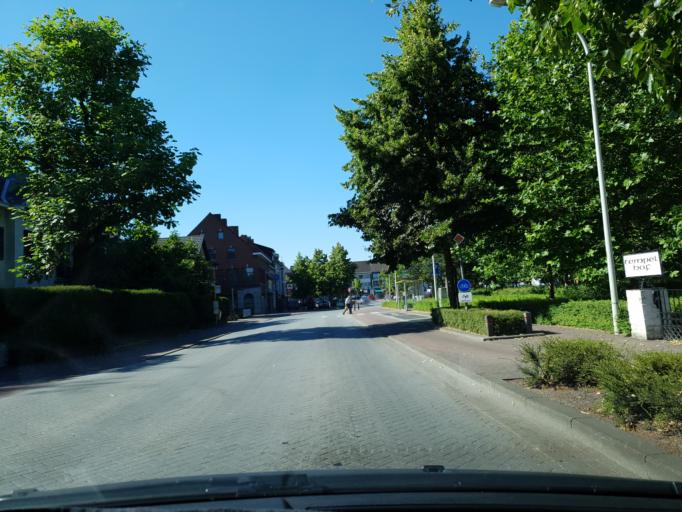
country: BE
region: Flanders
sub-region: Provincie Antwerpen
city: Beerse
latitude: 51.3179
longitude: 4.8554
